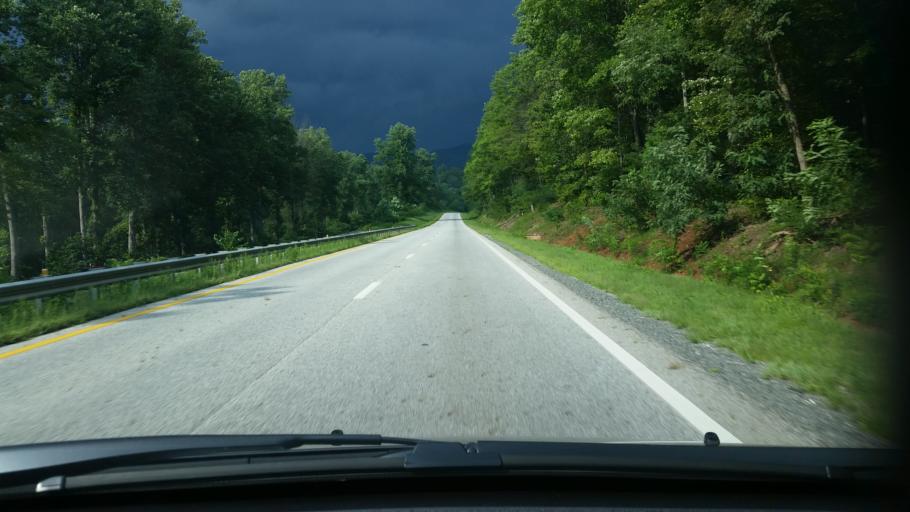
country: US
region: Virginia
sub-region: Nelson County
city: Nellysford
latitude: 37.8328
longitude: -78.8336
